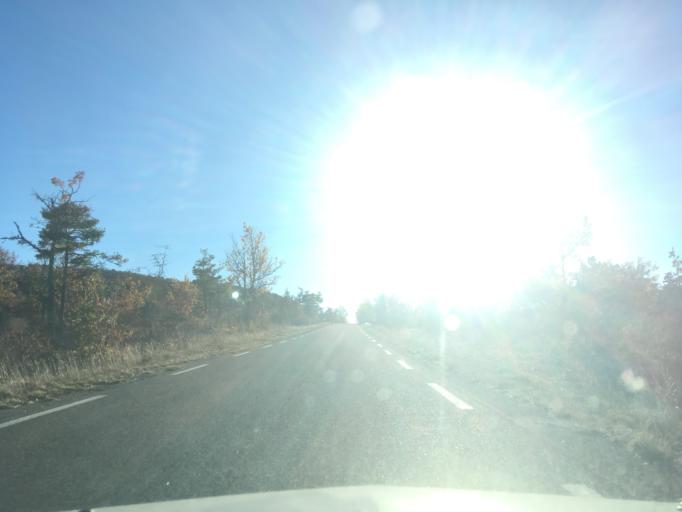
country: FR
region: Provence-Alpes-Cote d'Azur
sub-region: Departement du Var
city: Montferrat
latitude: 43.7383
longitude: 6.4352
